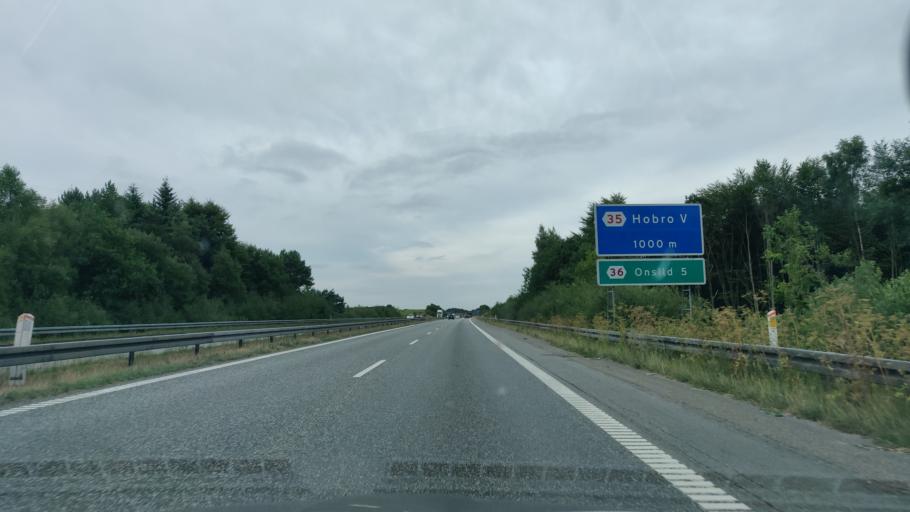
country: DK
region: North Denmark
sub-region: Mariagerfjord Kommune
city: Hobro
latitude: 56.6379
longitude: 9.7362
